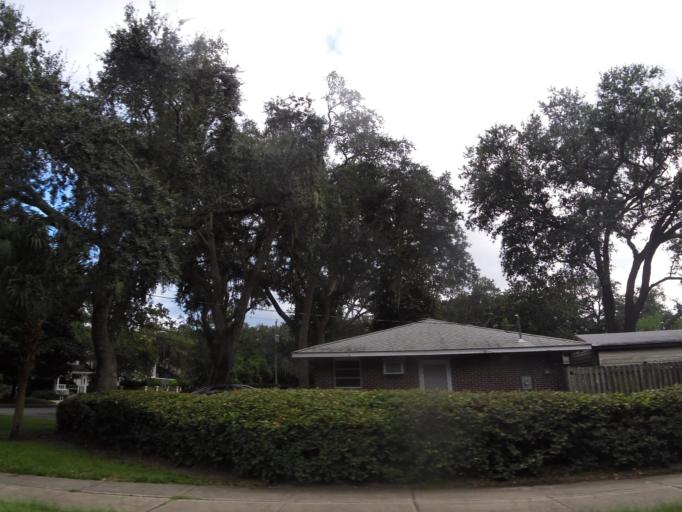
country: US
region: Georgia
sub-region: Glynn County
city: Saint Simons Island
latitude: 31.1576
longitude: -81.3835
